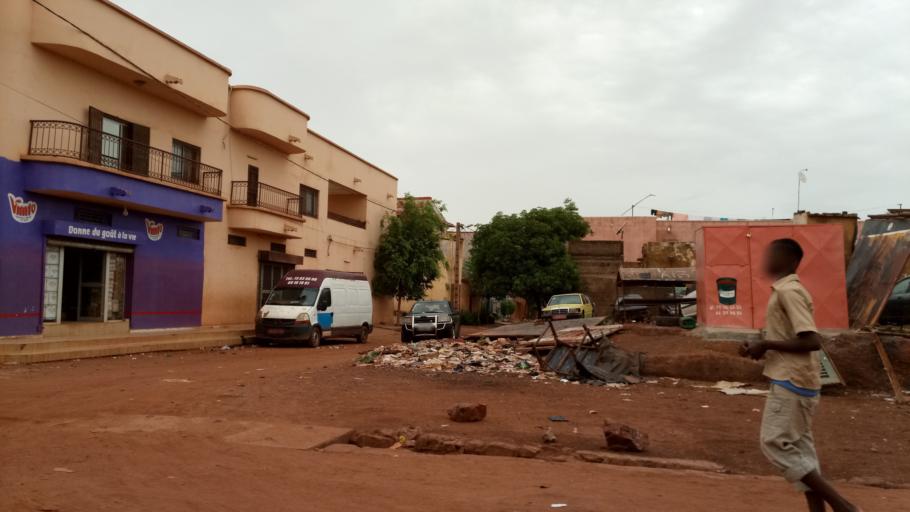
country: ML
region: Bamako
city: Bamako
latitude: 12.5828
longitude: -8.0095
